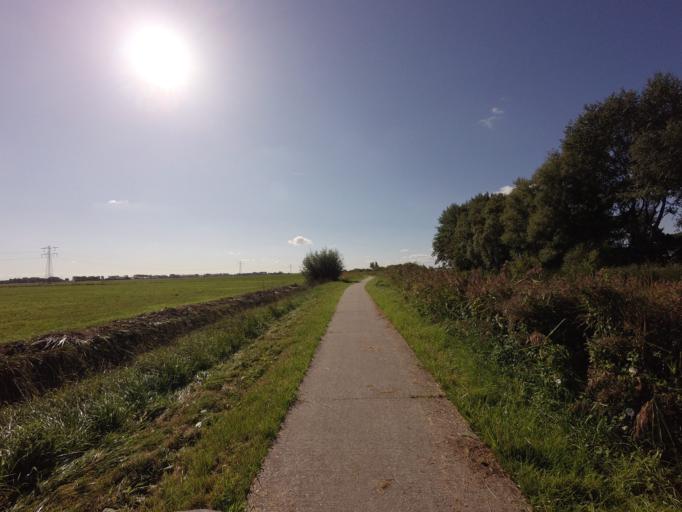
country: NL
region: Friesland
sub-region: Gemeente Boarnsterhim
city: Reduzum
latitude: 53.1485
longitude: 5.7637
